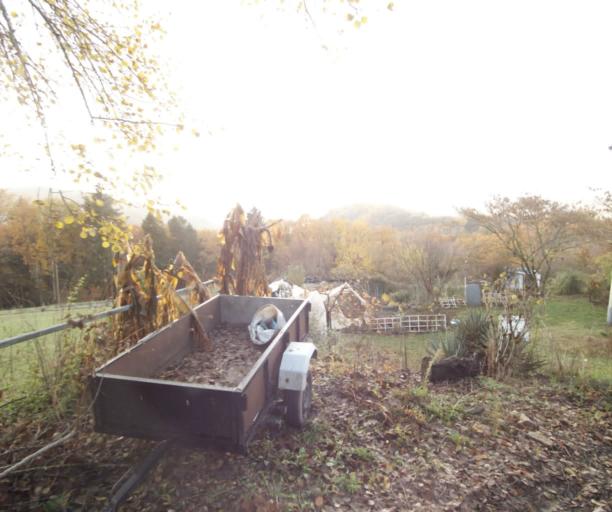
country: FR
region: Limousin
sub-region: Departement de la Correze
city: Cornil
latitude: 45.2161
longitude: 1.6738
